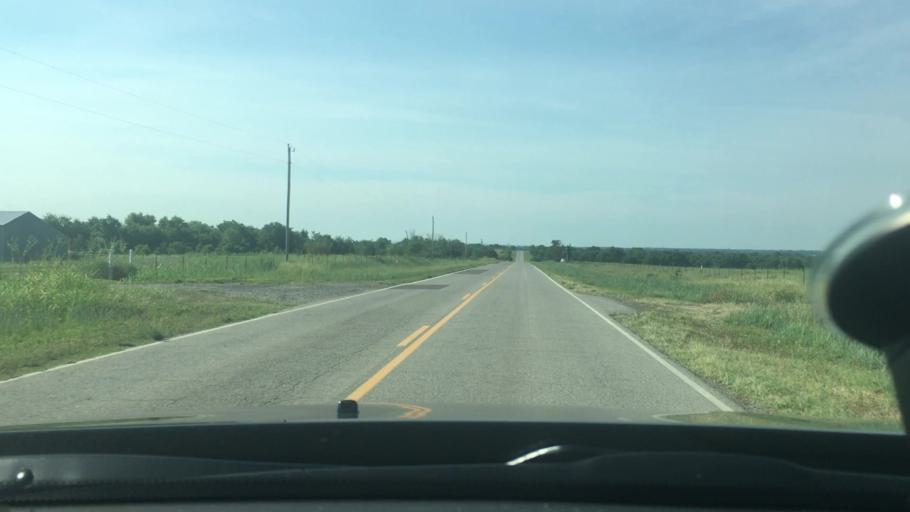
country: US
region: Oklahoma
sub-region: Garvin County
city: Maysville
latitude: 34.6624
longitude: -97.4053
